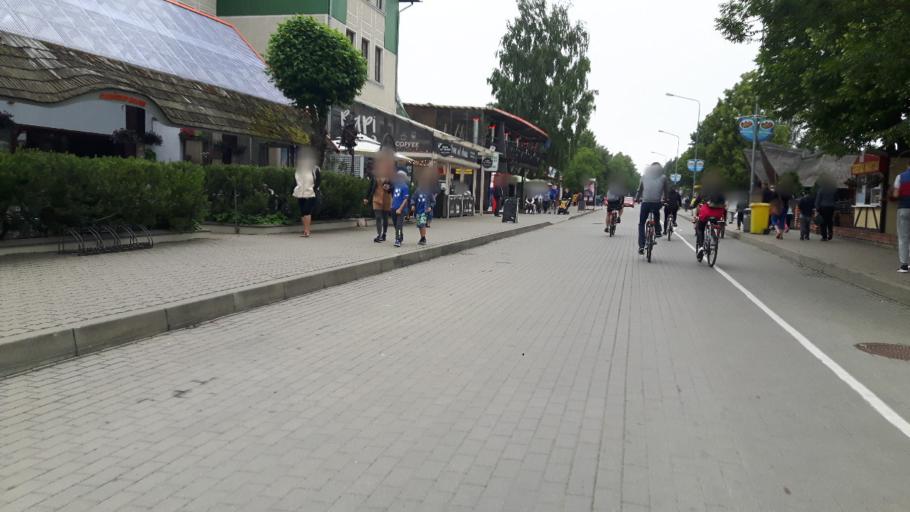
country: LT
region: Klaipedos apskritis
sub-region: Palanga
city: Sventoji
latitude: 56.0302
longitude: 21.0809
